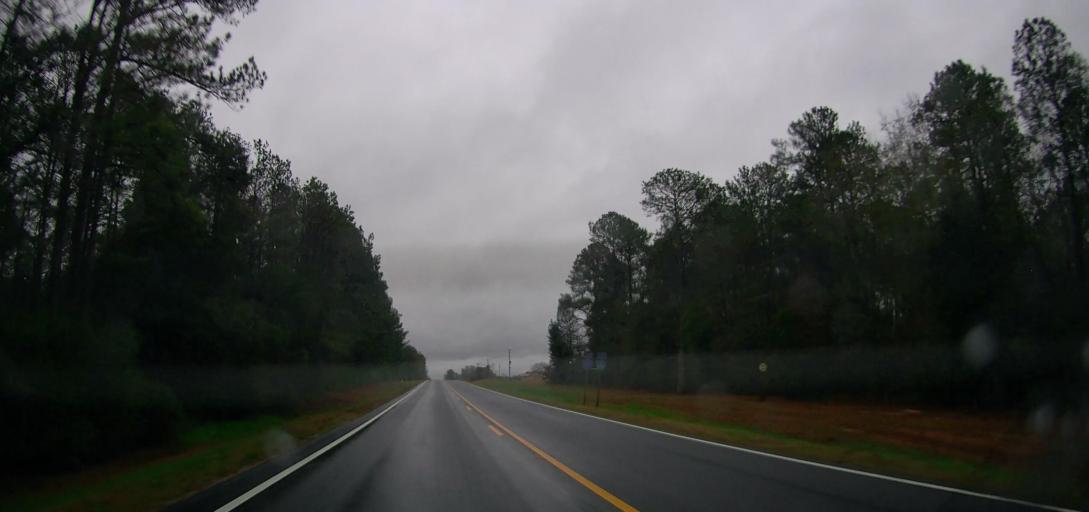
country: US
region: Alabama
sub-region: Bibb County
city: Centreville
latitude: 32.8107
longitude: -86.9279
